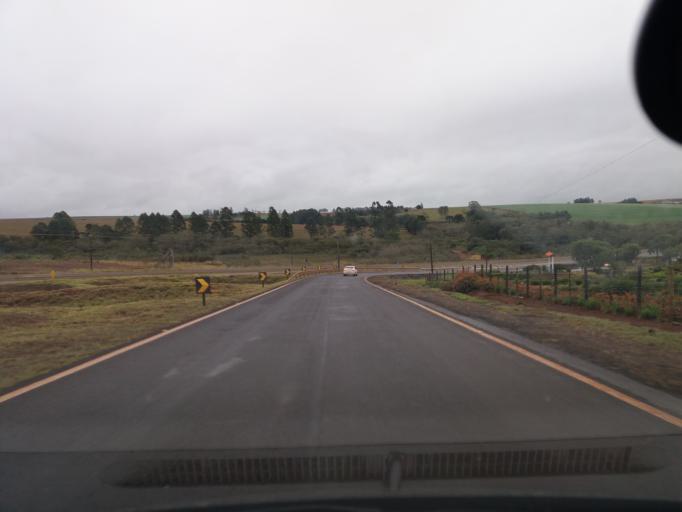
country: BR
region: Parana
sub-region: Campo Mourao
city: Campo Mourao
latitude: -23.9872
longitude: -52.3556
